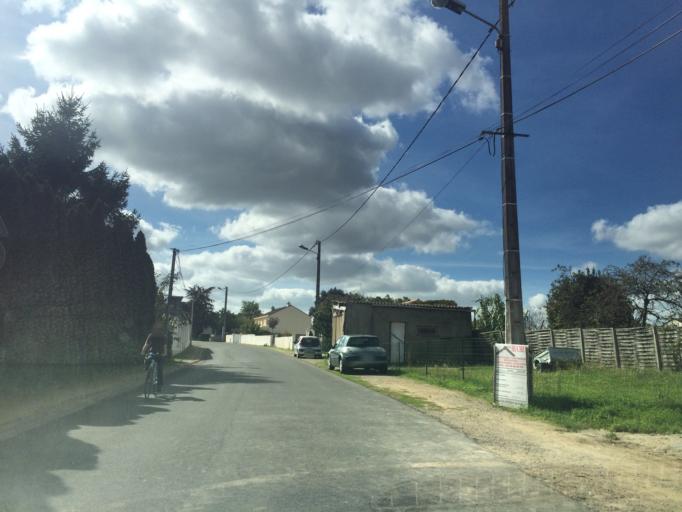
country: FR
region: Pays de la Loire
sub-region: Departement de la Loire-Atlantique
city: Chemere
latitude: 47.1211
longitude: -1.9132
